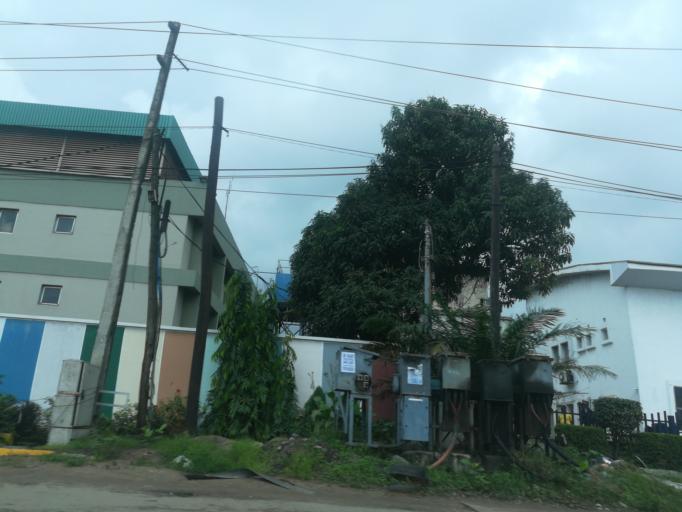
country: NG
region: Lagos
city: Agege
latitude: 6.6133
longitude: 3.3358
